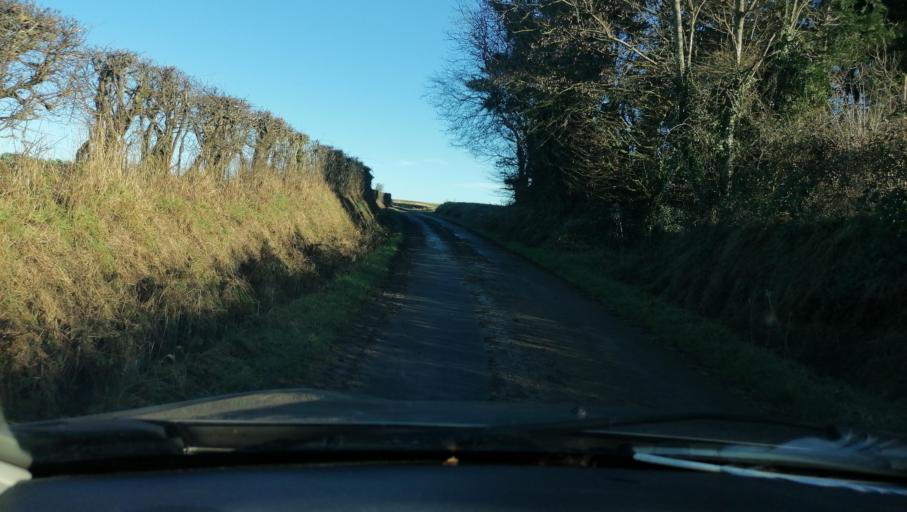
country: FR
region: Nord-Pas-de-Calais
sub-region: Departement du Nord
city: Ferriere-la-Grande
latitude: 50.2144
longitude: 4.0451
